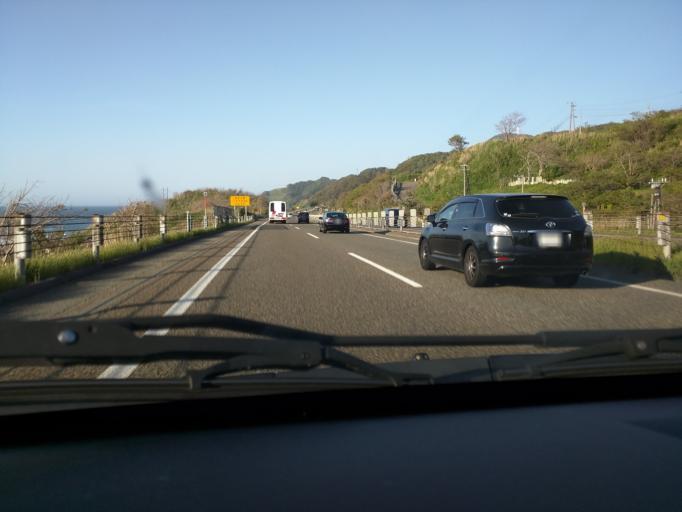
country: JP
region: Niigata
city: Kashiwazaki
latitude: 37.3076
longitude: 138.4217
